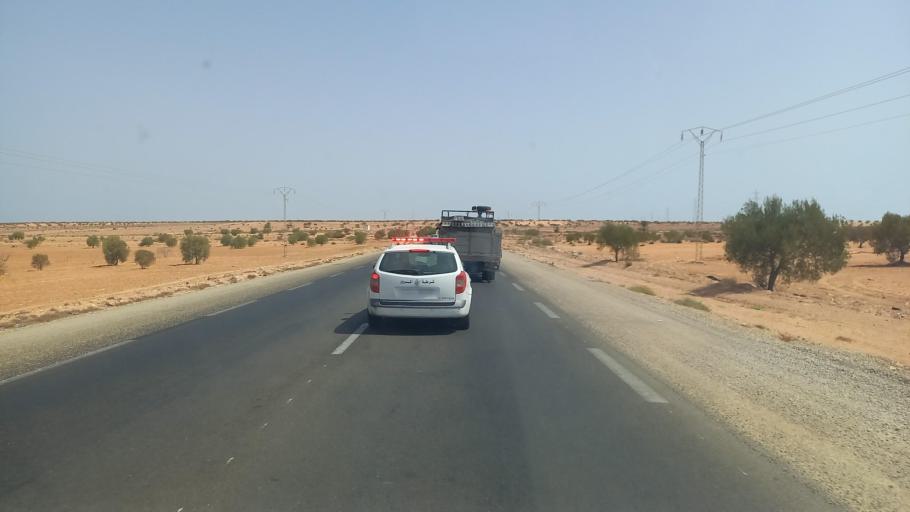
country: TN
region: Madanin
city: Zarzis
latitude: 33.4088
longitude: 10.8625
